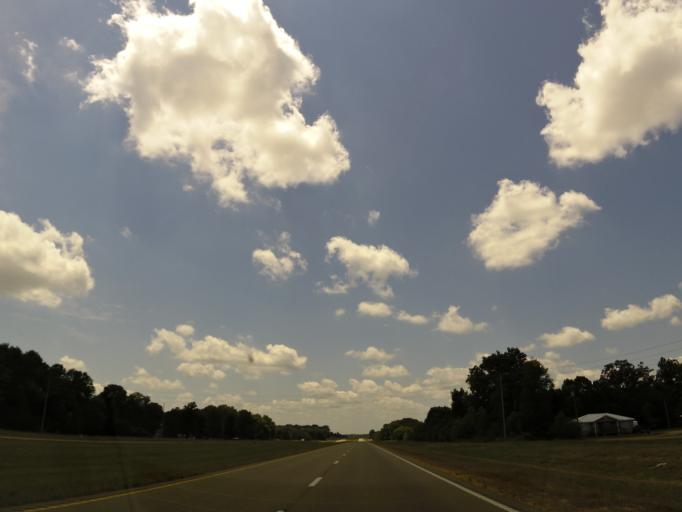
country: US
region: Mississippi
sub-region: Lee County
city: Verona
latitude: 34.2213
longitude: -88.8494
